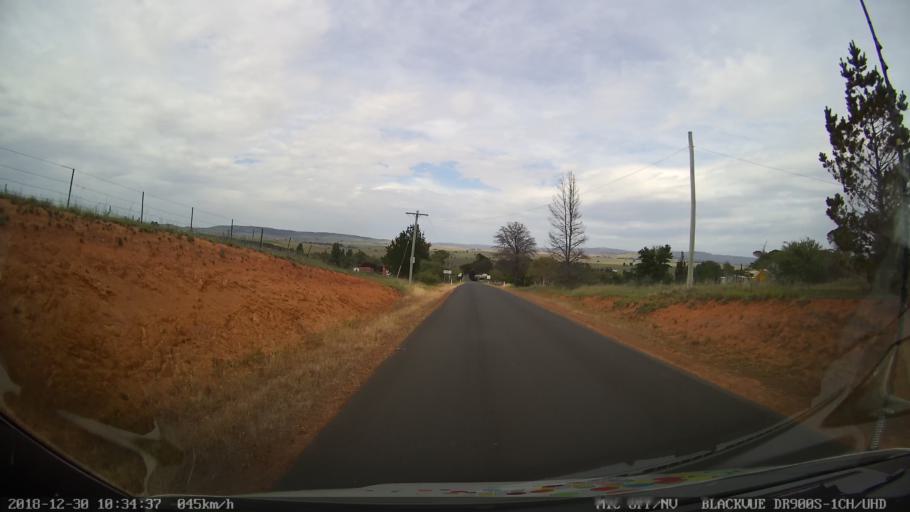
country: AU
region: New South Wales
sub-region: Snowy River
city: Berridale
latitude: -36.5013
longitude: 148.8394
